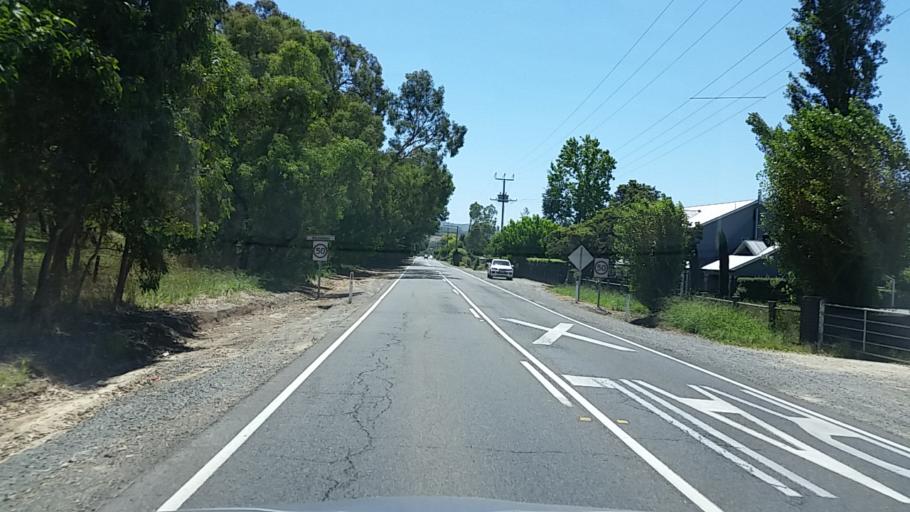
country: AU
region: South Australia
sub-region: Adelaide Hills
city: Balhannah
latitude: -34.9966
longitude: 138.8306
